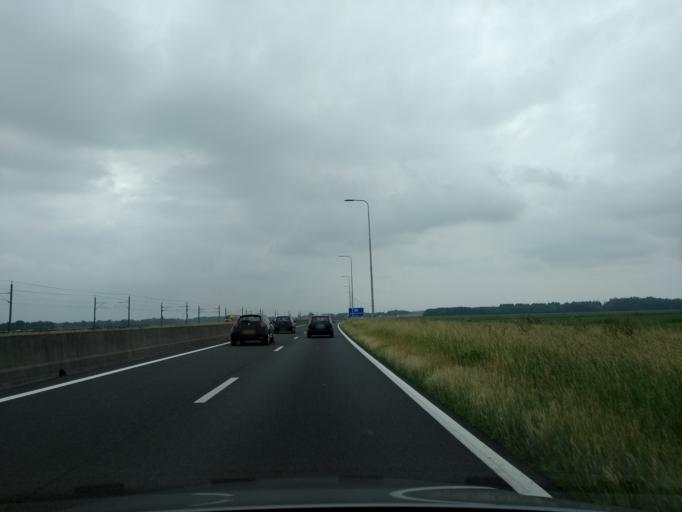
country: NL
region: Gelderland
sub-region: Gemeente Hattem
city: Hattem
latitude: 52.4987
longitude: 6.0054
